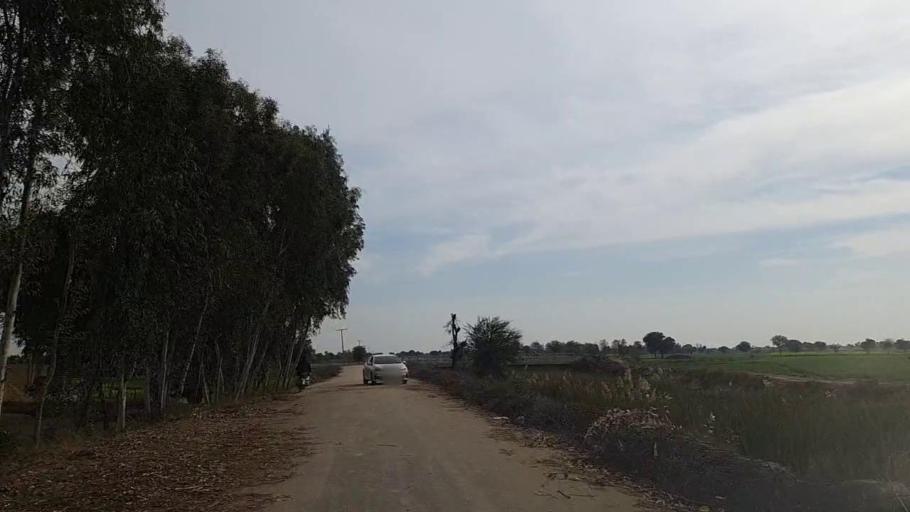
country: PK
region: Sindh
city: Daur
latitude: 26.4232
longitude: 68.4847
